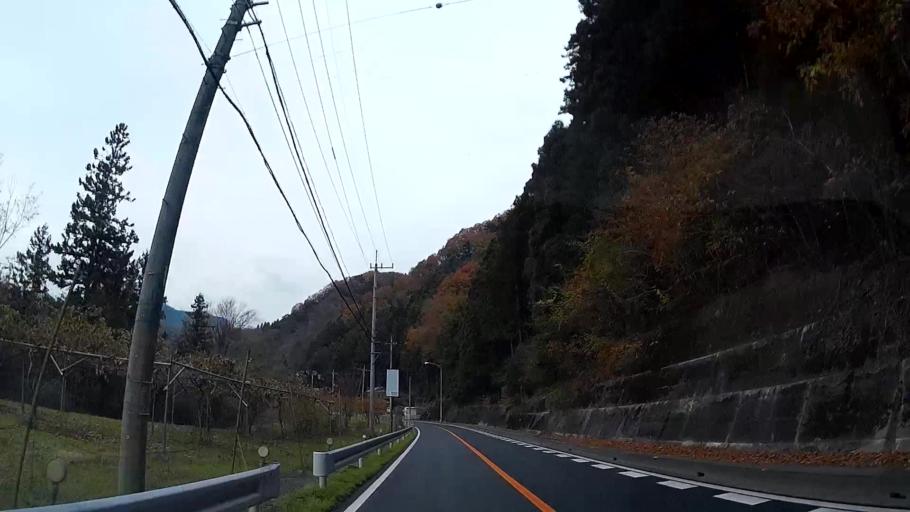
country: JP
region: Saitama
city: Chichibu
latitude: 35.9616
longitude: 139.0010
